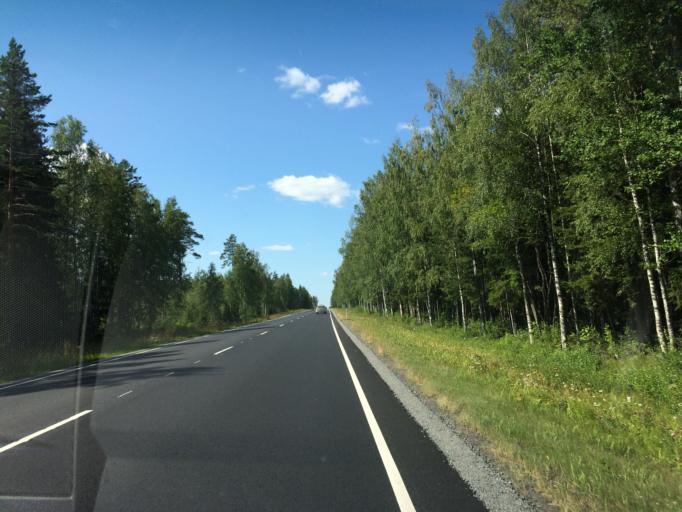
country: FI
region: Pirkanmaa
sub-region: Lounais-Pirkanmaa
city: Kiikoinen
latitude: 61.4744
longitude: 22.4853
